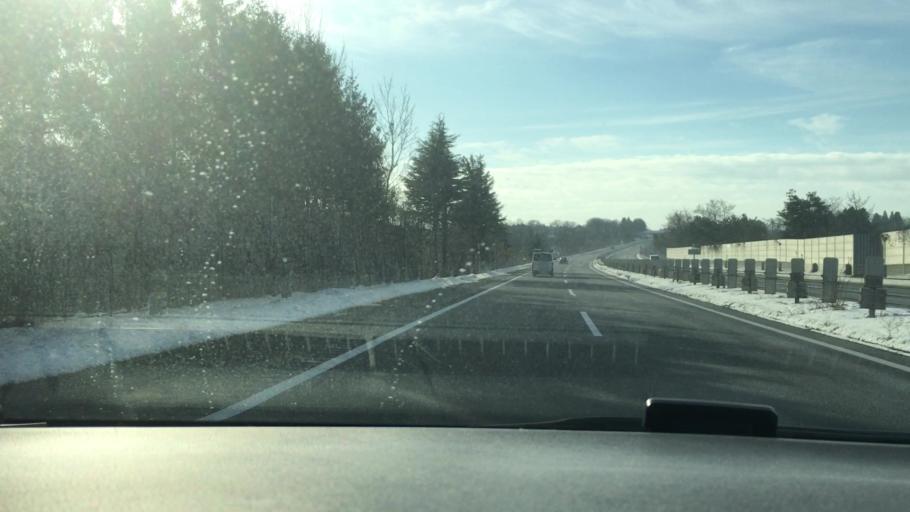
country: JP
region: Iwate
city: Hanamaki
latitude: 39.3785
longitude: 141.0928
